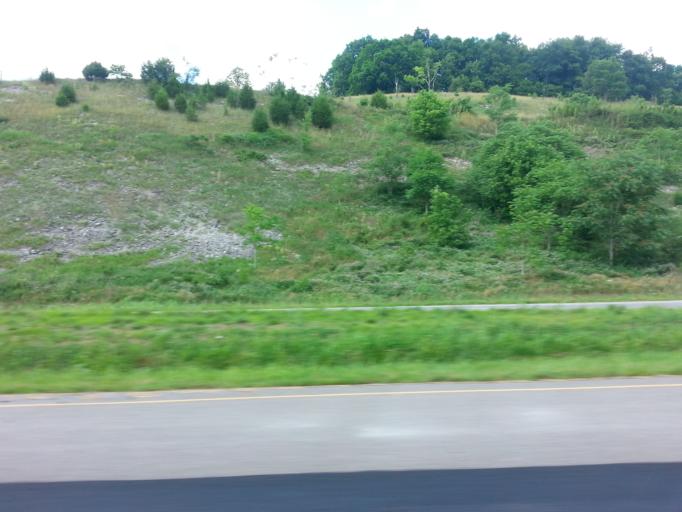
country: US
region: Virginia
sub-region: Lee County
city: Jonesville
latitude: 36.6740
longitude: -83.2090
